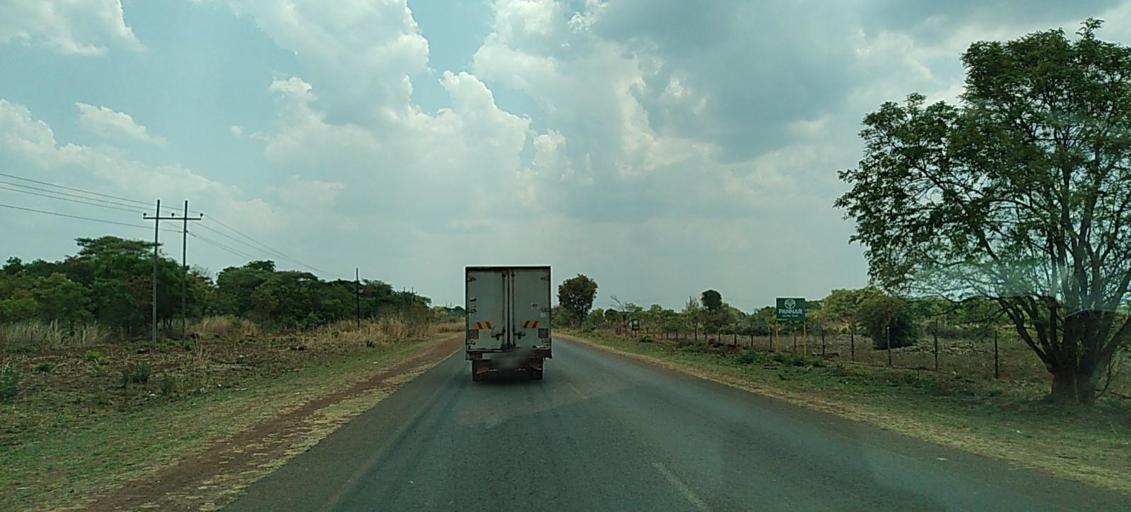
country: ZM
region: Copperbelt
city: Kalulushi
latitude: -12.8356
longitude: 27.9532
